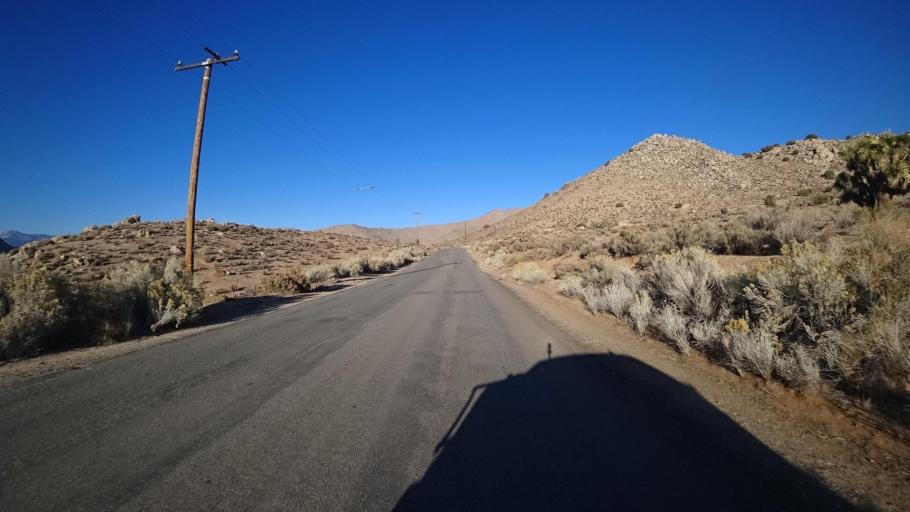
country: US
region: California
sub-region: Kern County
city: Weldon
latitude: 35.5896
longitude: -118.2413
